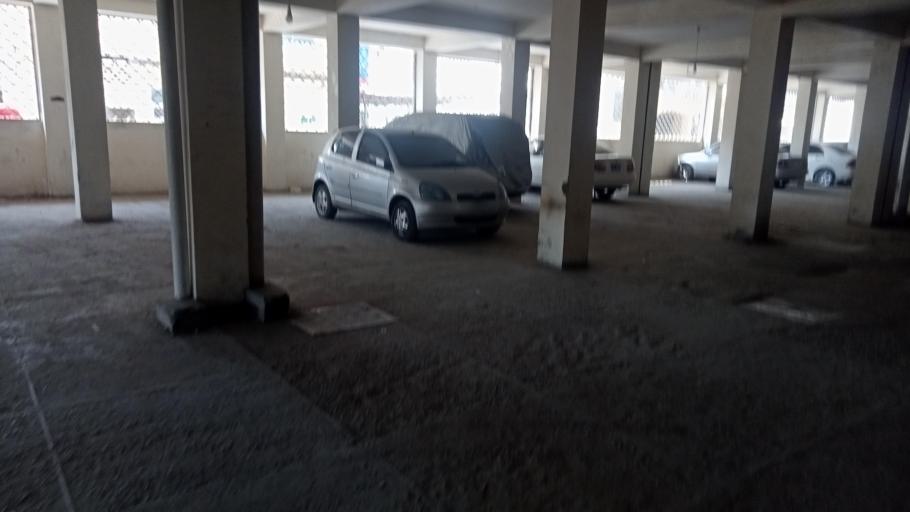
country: PK
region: Khyber Pakhtunkhwa
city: Mingora
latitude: 34.7698
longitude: 72.3596
